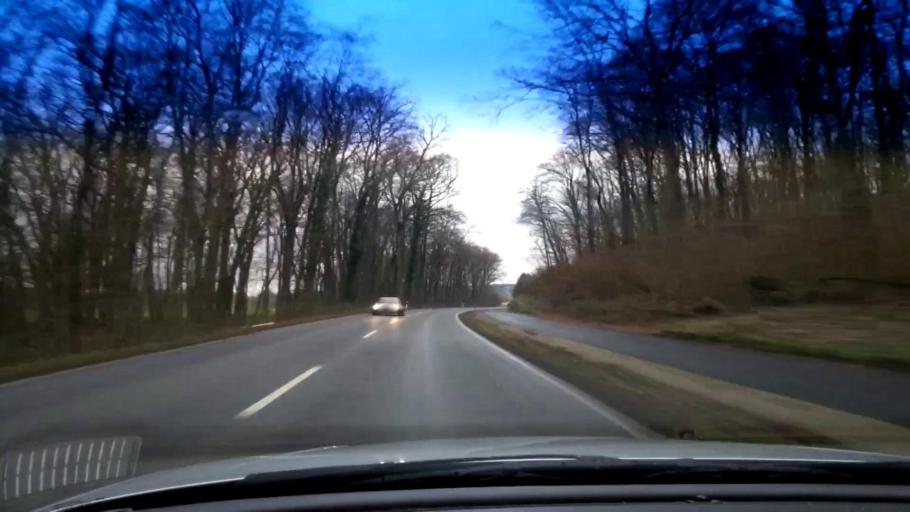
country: DE
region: Bavaria
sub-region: Upper Franconia
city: Pettstadt
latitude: 49.8484
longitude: 10.9285
